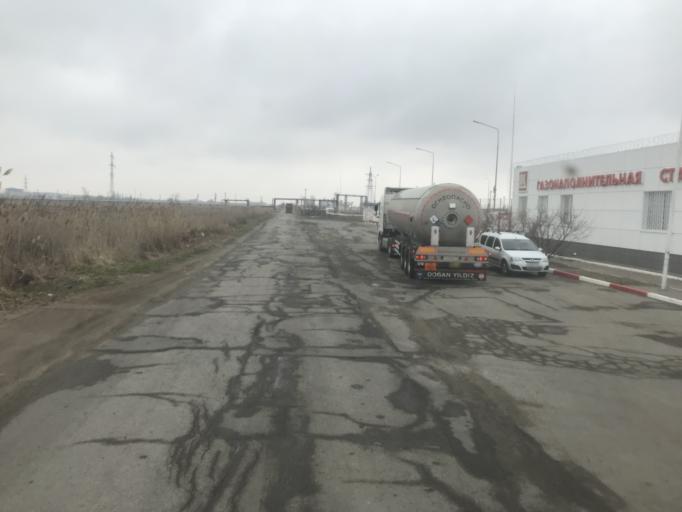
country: RU
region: Volgograd
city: Svetlyy Yar
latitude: 48.5120
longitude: 44.6367
